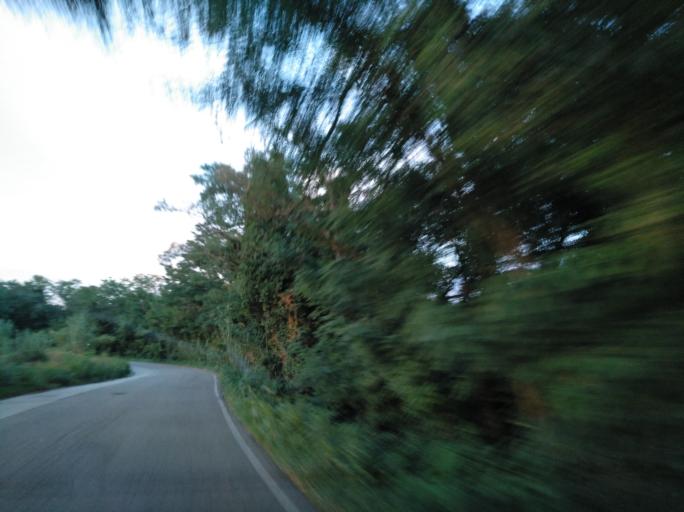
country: ES
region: Catalonia
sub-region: Provincia de Girona
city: Salt
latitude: 41.9598
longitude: 2.7956
